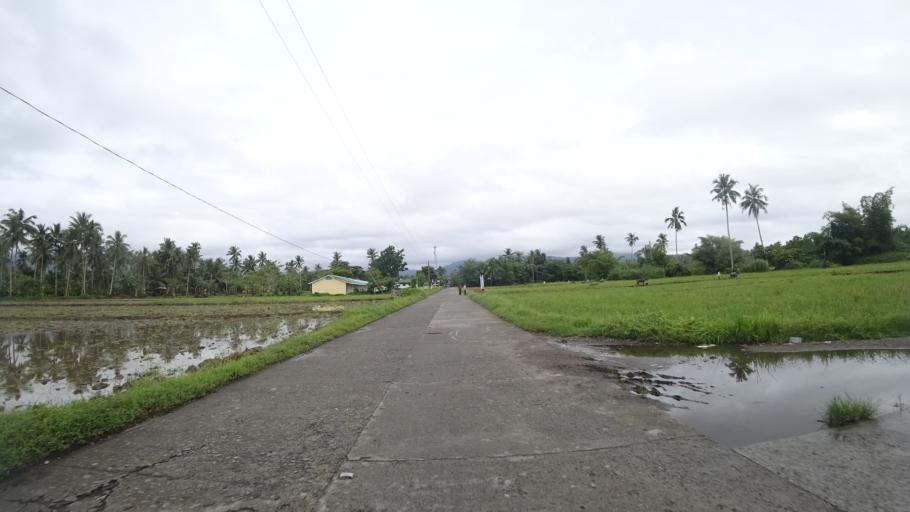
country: PH
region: Eastern Visayas
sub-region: Province of Leyte
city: Bugho
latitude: 10.8217
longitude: 124.9395
